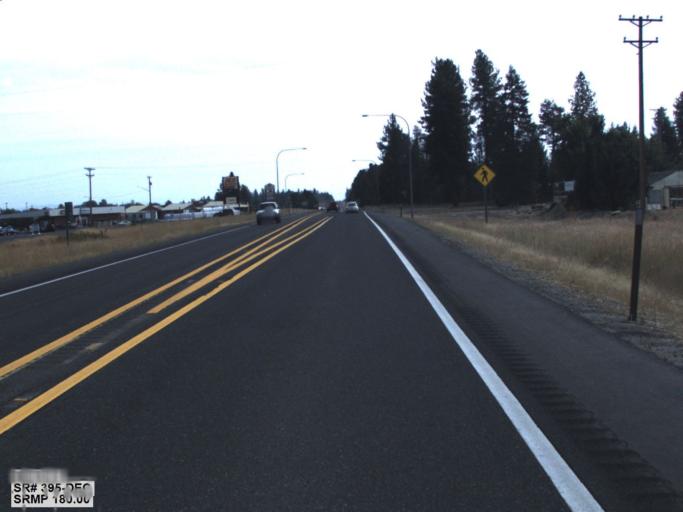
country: US
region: Washington
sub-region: Spokane County
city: Deer Park
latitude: 47.9484
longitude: -117.4828
